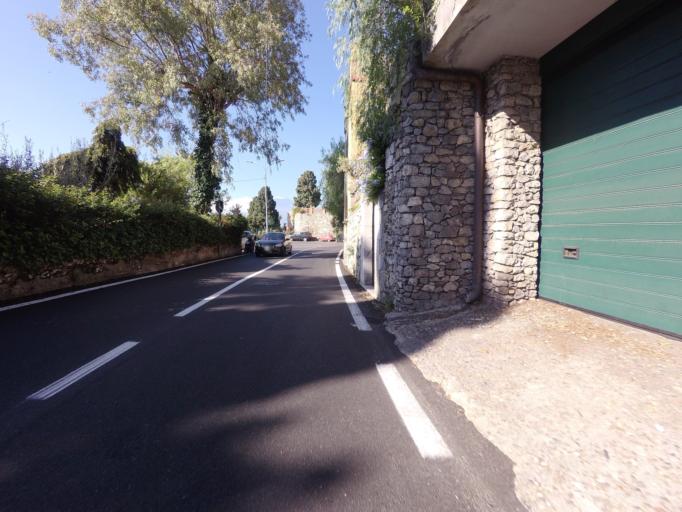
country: IT
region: Sicily
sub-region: Messina
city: Taormina
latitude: 37.8497
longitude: 15.2921
